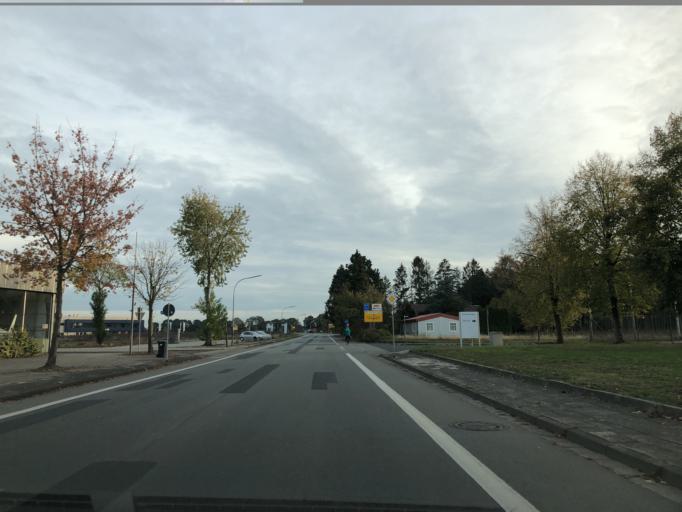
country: DE
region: Lower Saxony
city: Lehe
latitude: 53.0415
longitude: 7.3253
